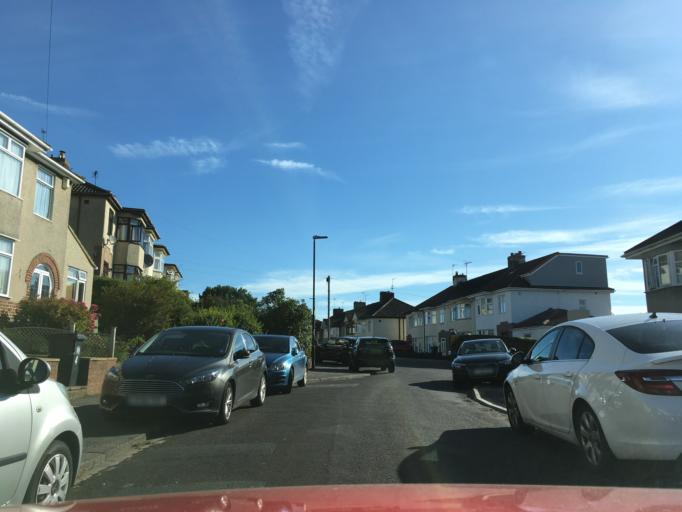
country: GB
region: England
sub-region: Bath and North East Somerset
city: Whitchurch
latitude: 51.4323
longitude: -2.5513
